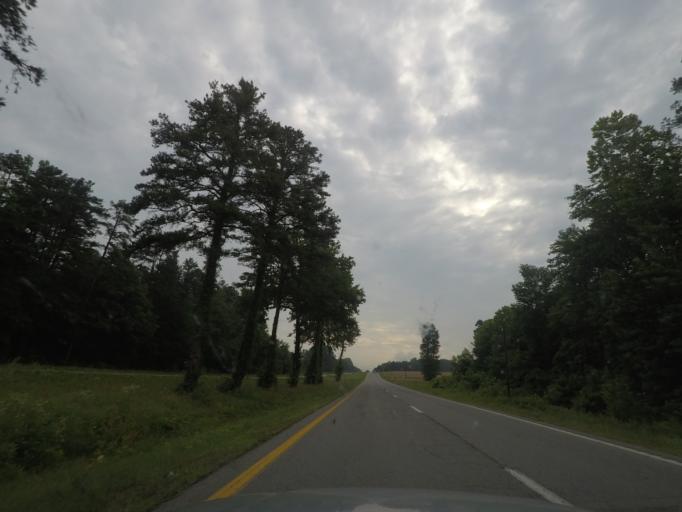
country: US
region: Virginia
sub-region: Mecklenburg County
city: Chase City
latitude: 36.8875
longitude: -78.5522
